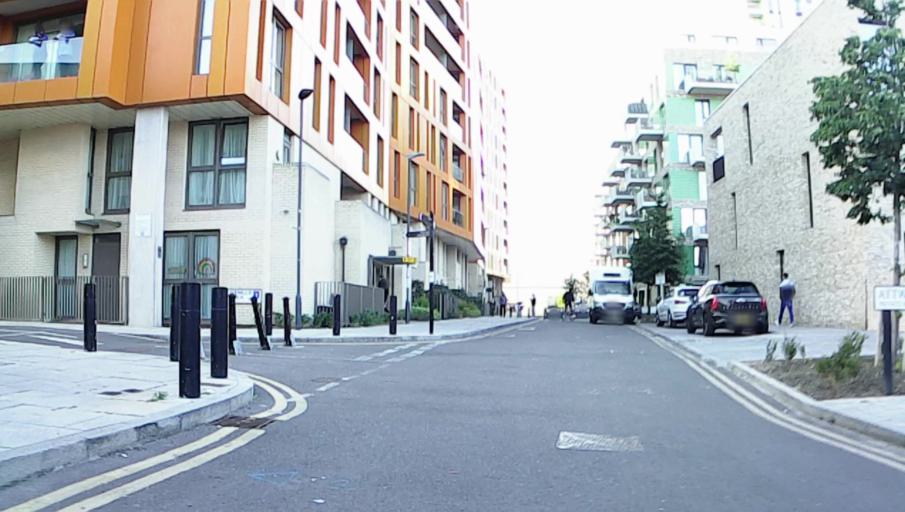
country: GB
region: England
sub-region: Greater London
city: Blackheath
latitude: 51.4894
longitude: 0.0047
